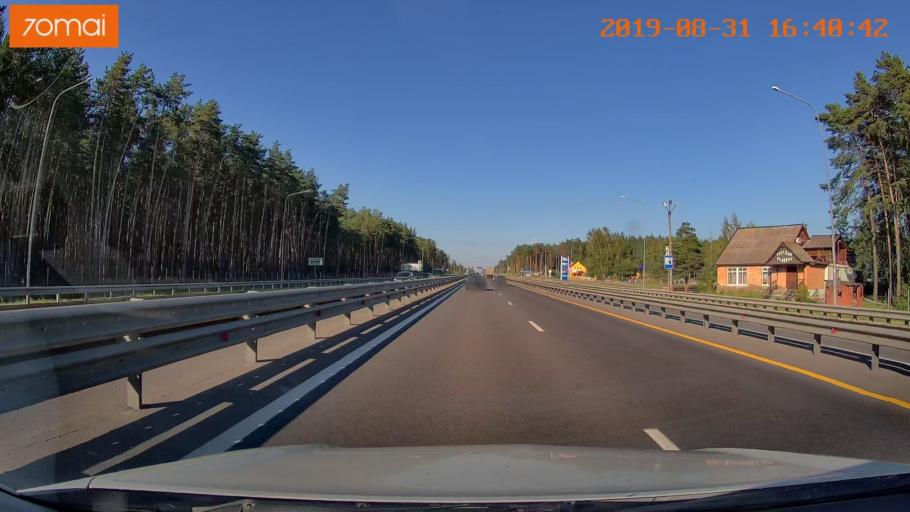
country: RU
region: Kaluga
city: Kurovskoye
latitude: 54.5694
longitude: 36.0539
